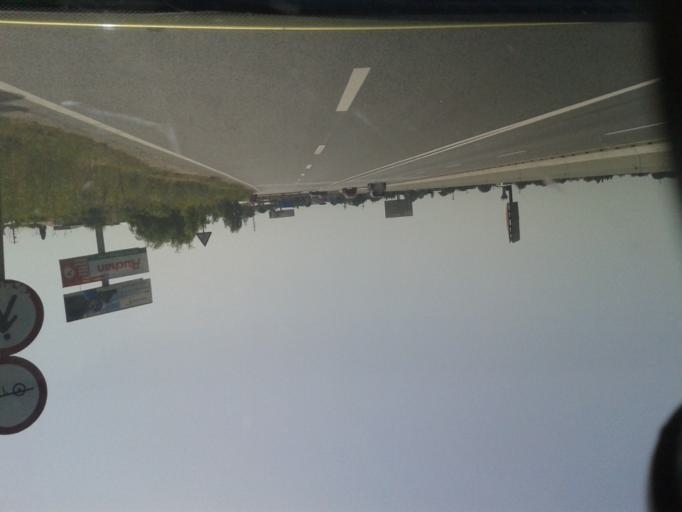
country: RO
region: Prahova
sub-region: Comuna Barcanesti
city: Tatarani
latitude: 44.8849
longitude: 26.0295
